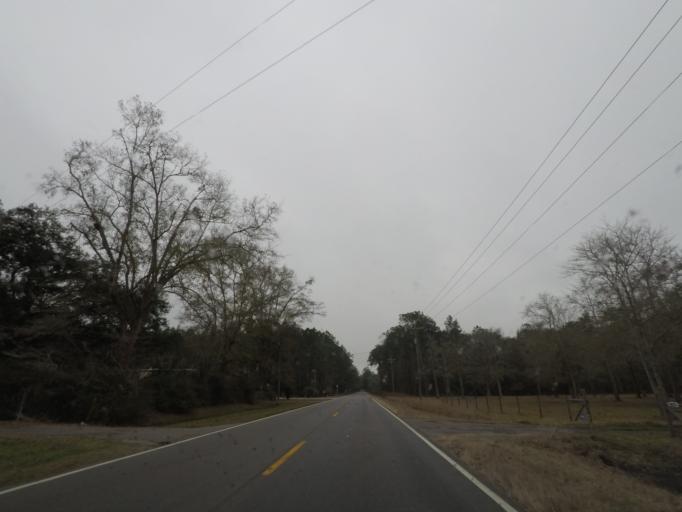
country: US
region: South Carolina
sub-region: Charleston County
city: Ravenel
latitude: 32.7436
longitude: -80.3490
